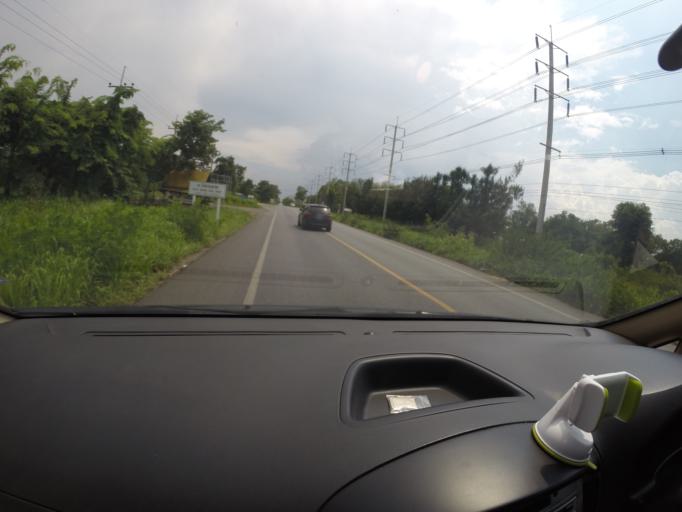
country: TH
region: Nakhon Ratchasima
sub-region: Amphoe Thepharak
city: Thepharak
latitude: 15.1141
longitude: 101.4651
